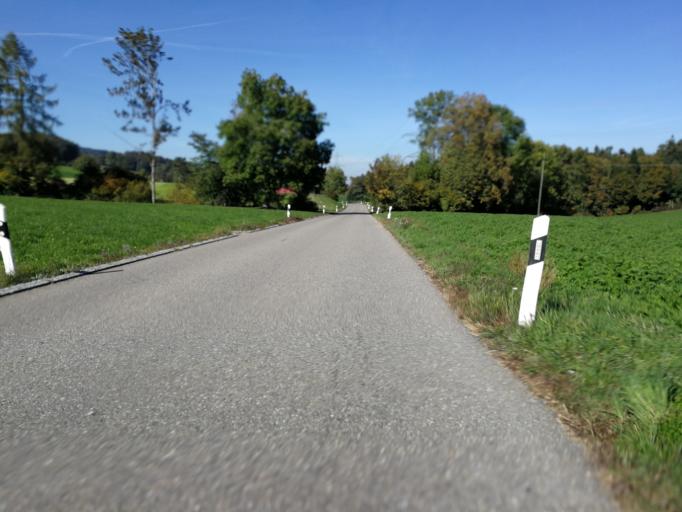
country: CH
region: Zurich
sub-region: Bezirk Uster
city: Hinteregg
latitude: 47.3150
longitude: 8.6761
